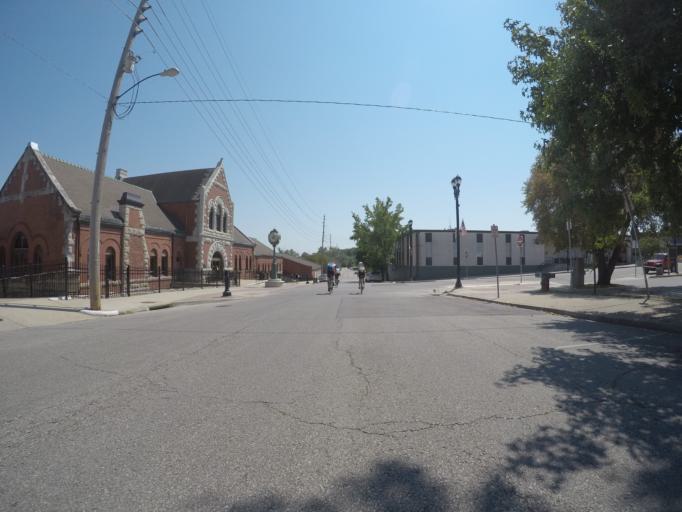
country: US
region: Kansas
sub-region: Leavenworth County
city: Leavenworth
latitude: 39.3190
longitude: -94.9096
